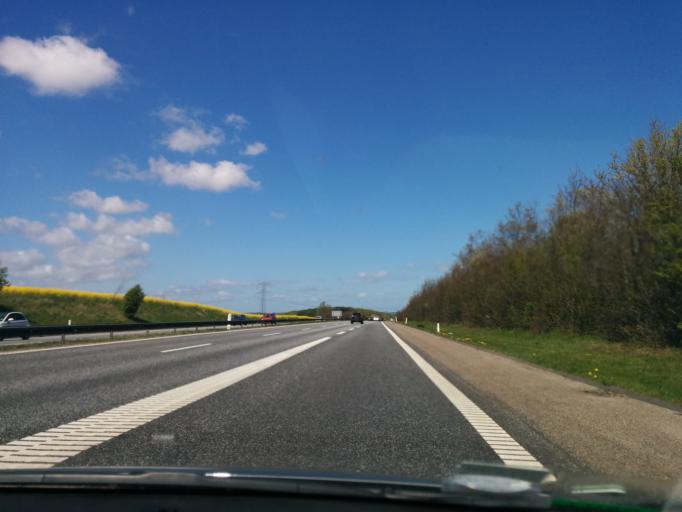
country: DK
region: Central Jutland
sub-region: Skanderborg Kommune
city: Horning
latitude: 56.1142
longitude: 10.0389
